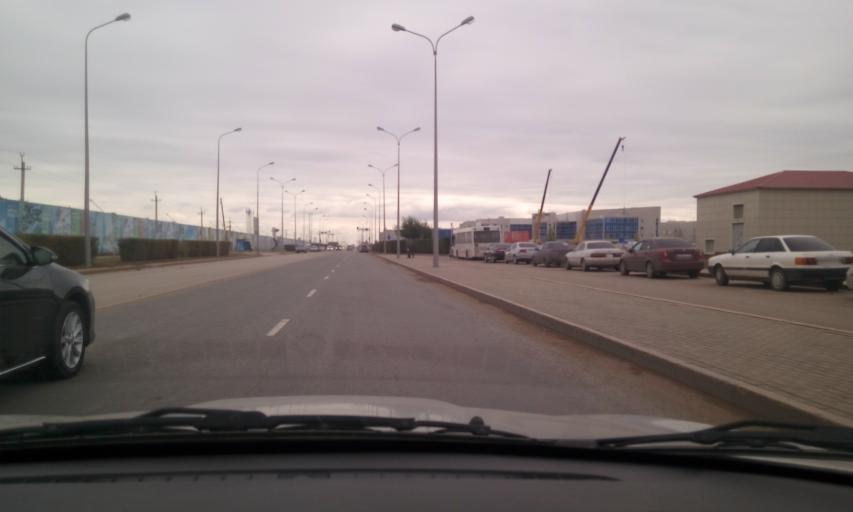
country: KZ
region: Astana Qalasy
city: Astana
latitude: 51.0860
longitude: 71.4037
